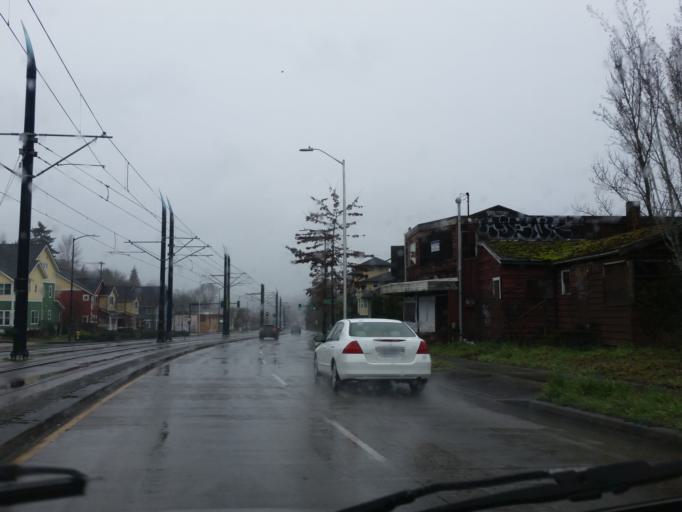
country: US
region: Washington
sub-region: King County
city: Seattle
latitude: 47.5666
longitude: -122.2968
